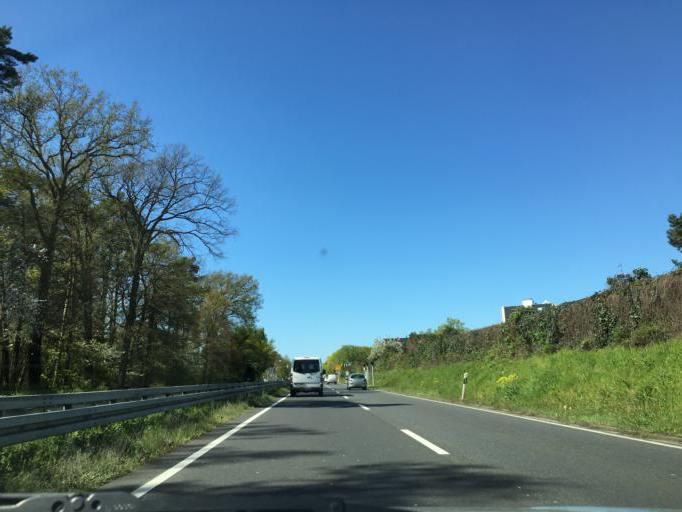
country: DE
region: Hesse
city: Obertshausen
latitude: 50.0736
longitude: 8.8610
